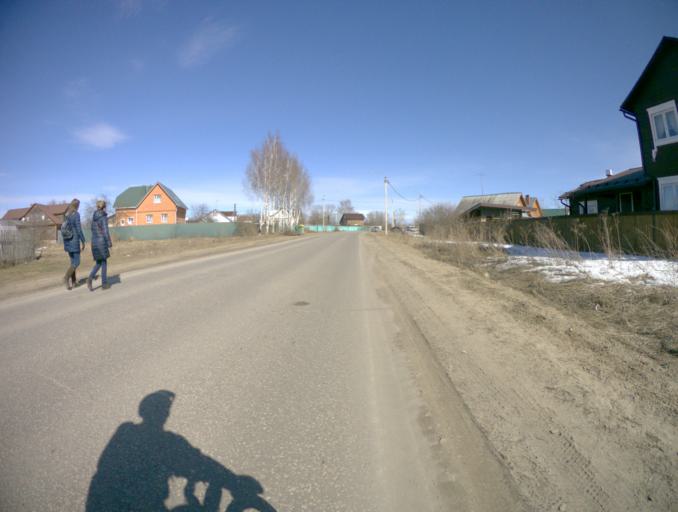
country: RU
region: Vladimir
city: Suzdal'
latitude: 56.4374
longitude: 40.4357
